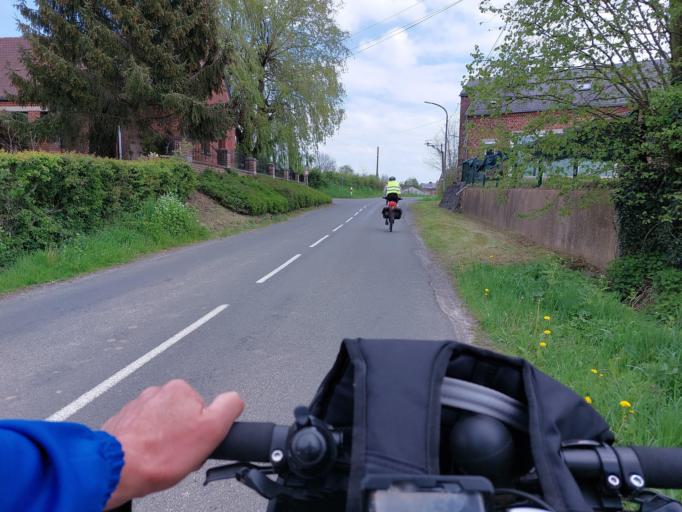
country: FR
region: Nord-Pas-de-Calais
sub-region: Departement du Nord
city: La Longueville
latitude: 50.2729
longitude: 3.8859
